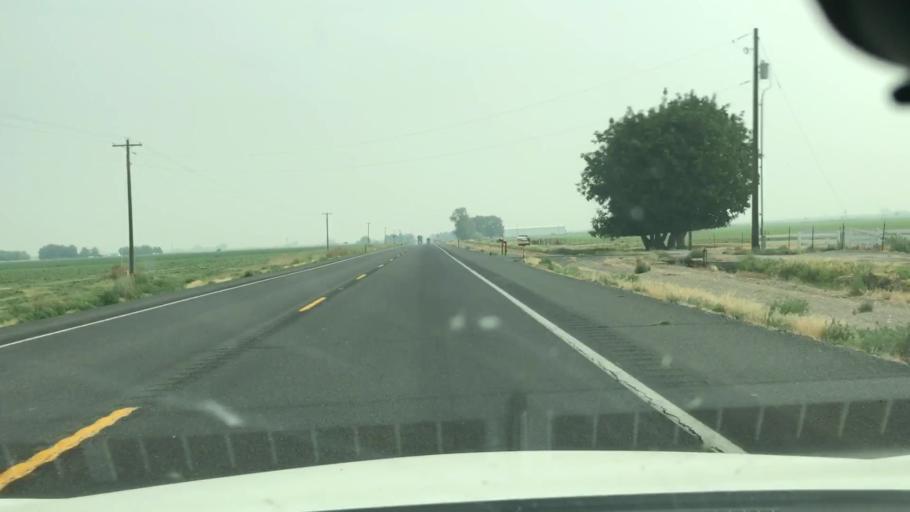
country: US
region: Washington
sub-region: Grant County
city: Quincy
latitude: 47.2342
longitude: -119.7785
